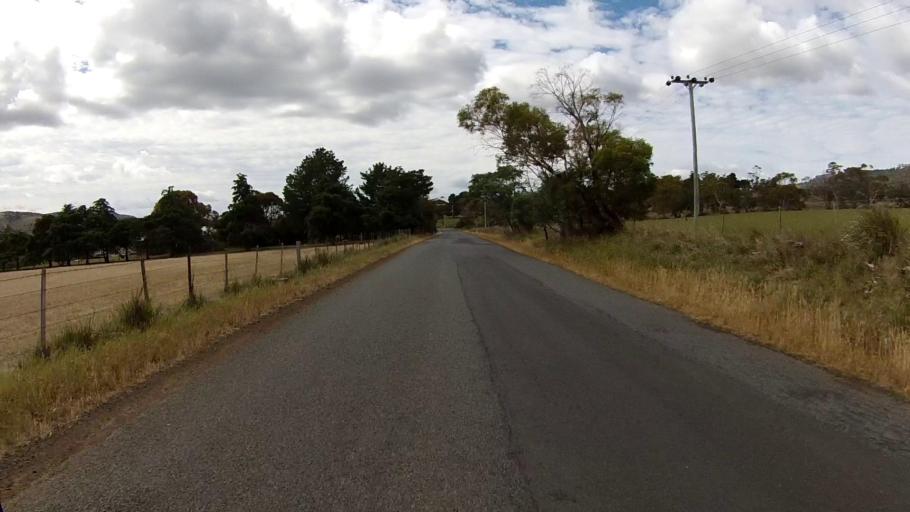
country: AU
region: Tasmania
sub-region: Clarence
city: Cambridge
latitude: -42.7699
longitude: 147.4094
